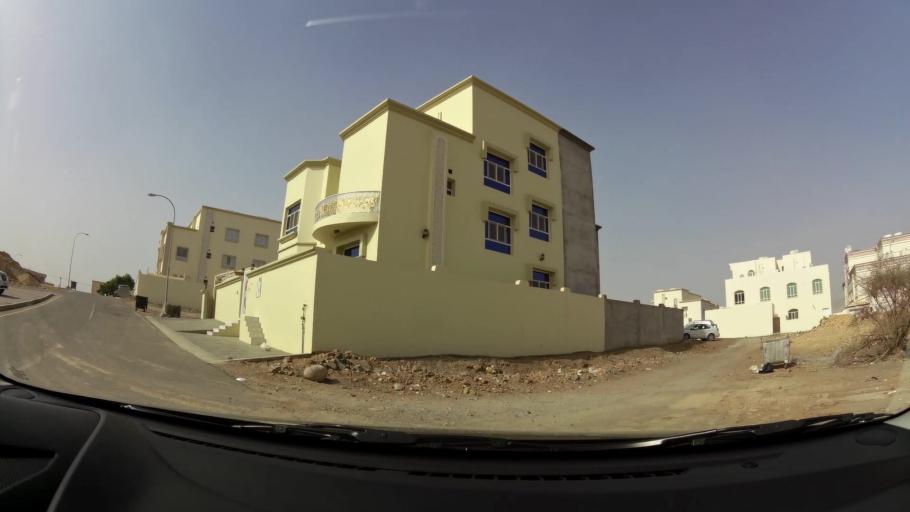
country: OM
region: Muhafazat Masqat
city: Bawshar
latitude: 23.5599
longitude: 58.3612
